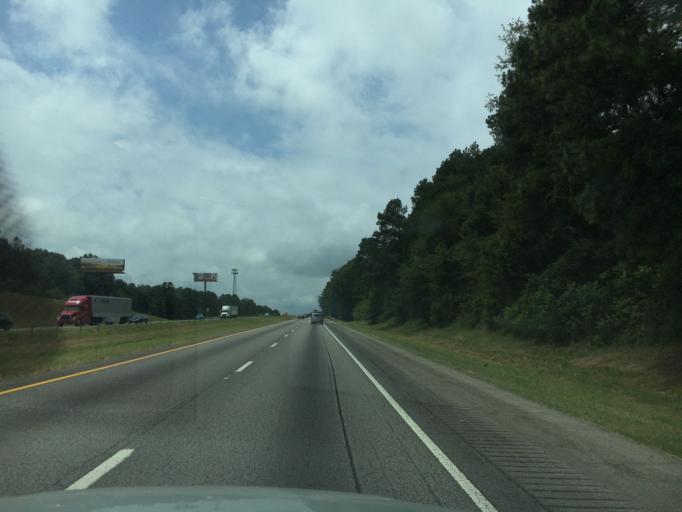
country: US
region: Georgia
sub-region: Banks County
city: Maysville
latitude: 34.1923
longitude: -83.5835
